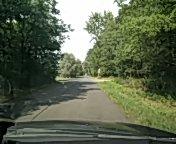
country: HU
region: Hajdu-Bihar
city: Hajdusamson
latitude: 47.5181
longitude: 21.7342
